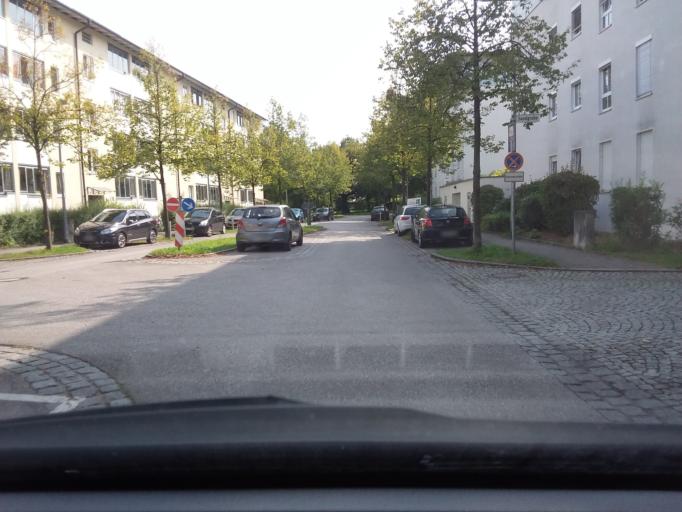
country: DE
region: Bavaria
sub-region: Upper Bavaria
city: Oberschleissheim
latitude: 48.2568
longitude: 11.5435
